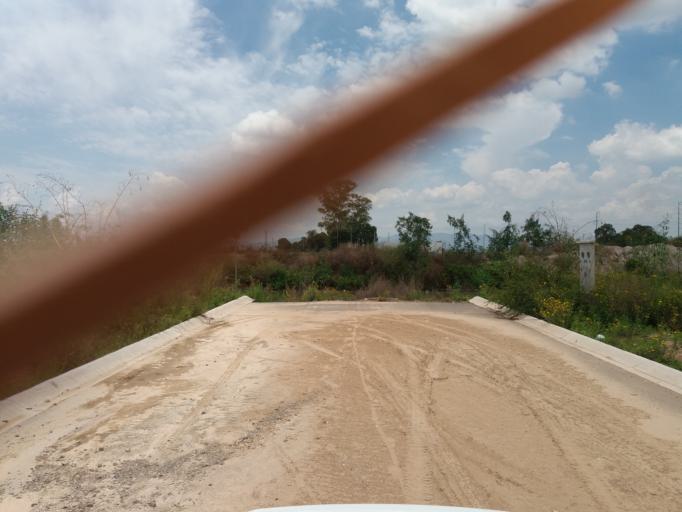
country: MX
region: Aguascalientes
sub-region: Aguascalientes
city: San Sebastian [Fraccionamiento]
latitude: 21.8117
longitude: -102.2688
